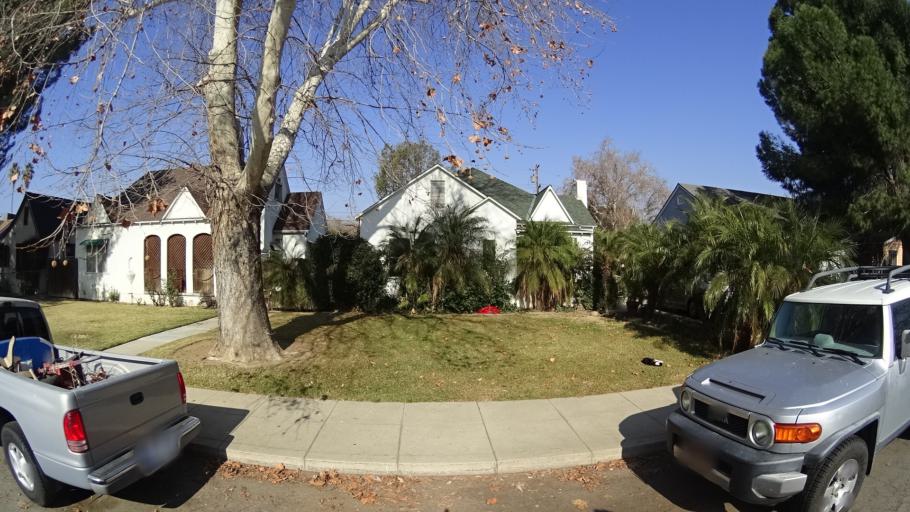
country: US
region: California
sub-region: Kern County
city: Bakersfield
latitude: 35.3867
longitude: -118.9978
